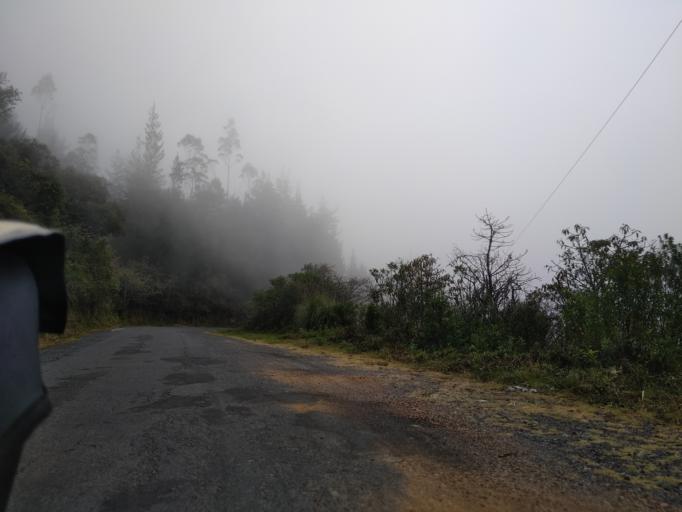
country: EC
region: Cotopaxi
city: Saquisili
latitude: -0.6872
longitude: -78.8324
